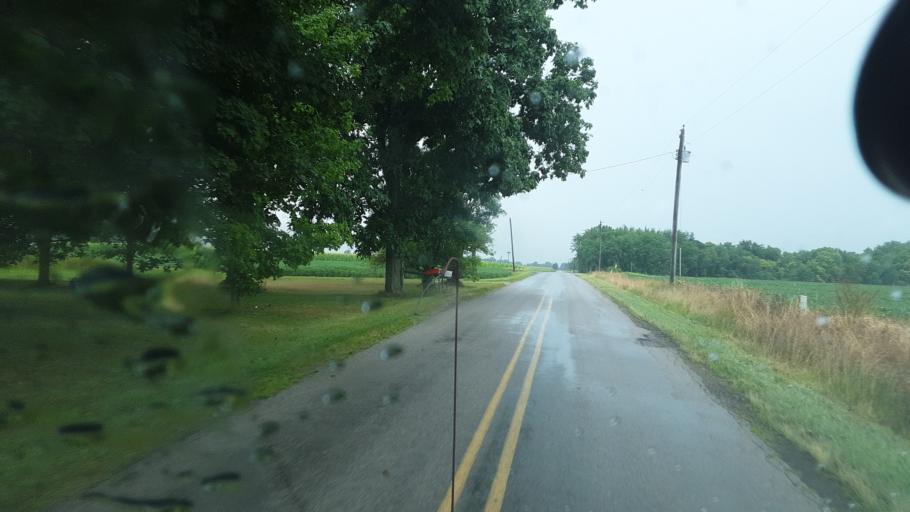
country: US
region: Ohio
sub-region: Williams County
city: Edgerton
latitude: 41.4893
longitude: -84.8147
